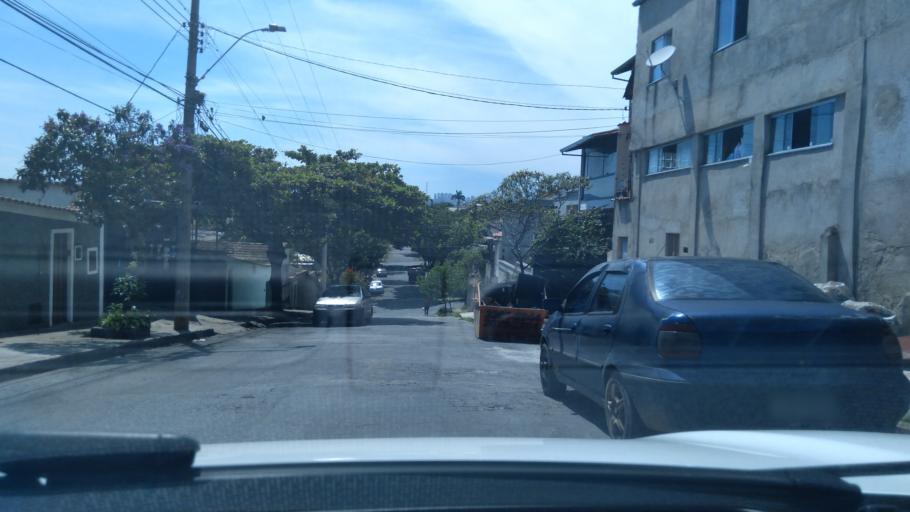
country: BR
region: Minas Gerais
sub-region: Contagem
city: Contagem
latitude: -19.9259
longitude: -44.0034
